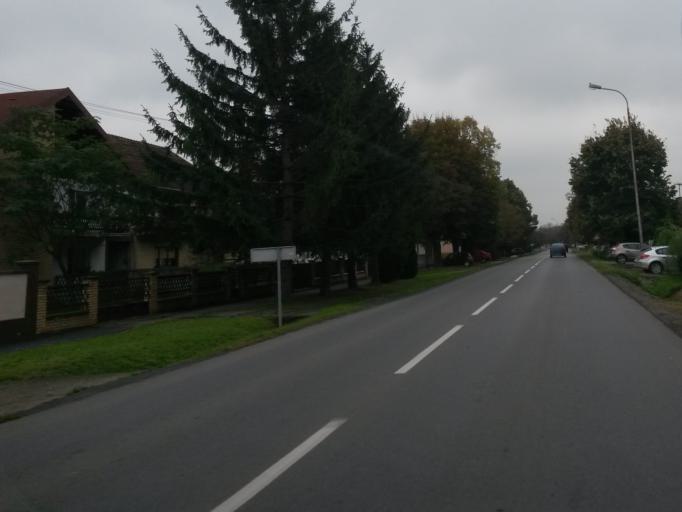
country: HR
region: Osjecko-Baranjska
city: Cepin
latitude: 45.5206
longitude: 18.5722
